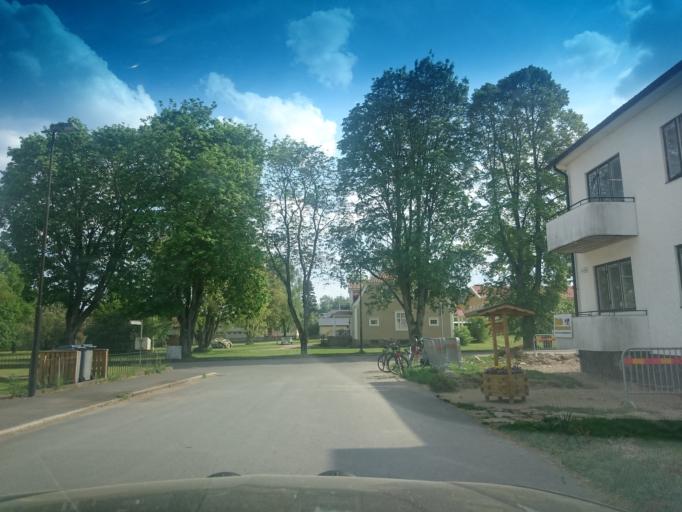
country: SE
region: Joenkoeping
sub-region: Vetlanda Kommun
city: Vetlanda
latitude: 57.4318
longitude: 15.0715
